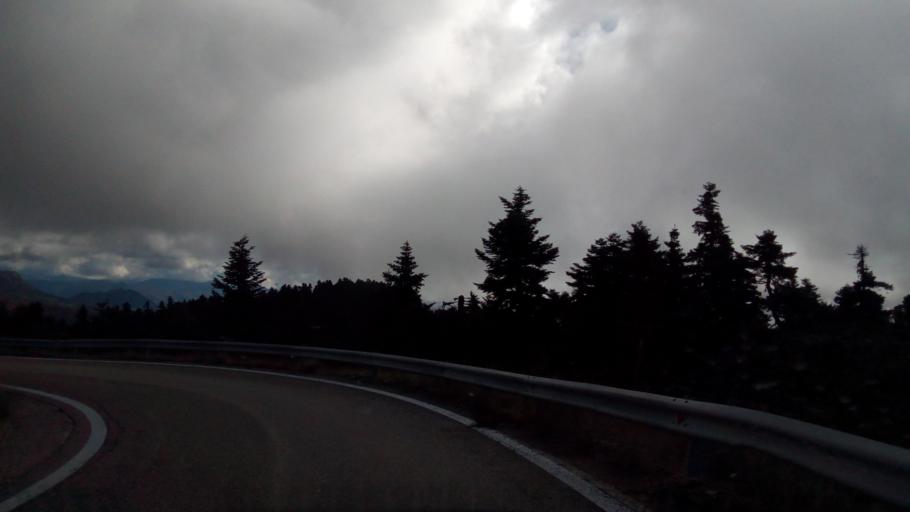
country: GR
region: West Greece
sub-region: Nomos Aitolias kai Akarnanias
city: Nafpaktos
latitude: 38.5864
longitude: 21.9598
